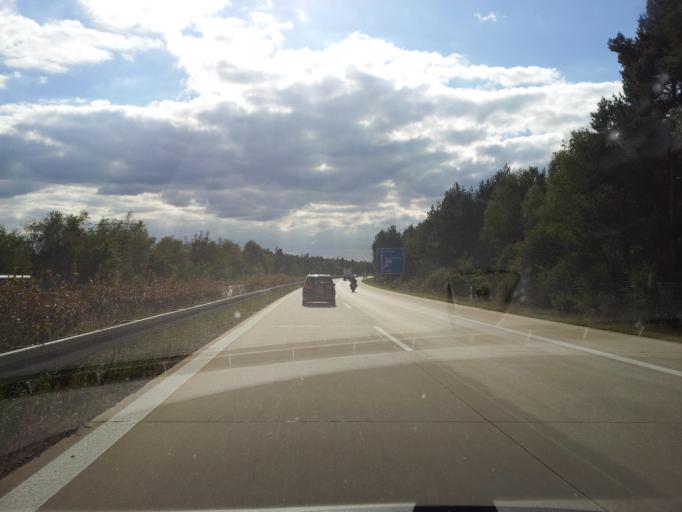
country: DE
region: Brandenburg
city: Schipkau
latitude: 51.4981
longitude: 13.9005
